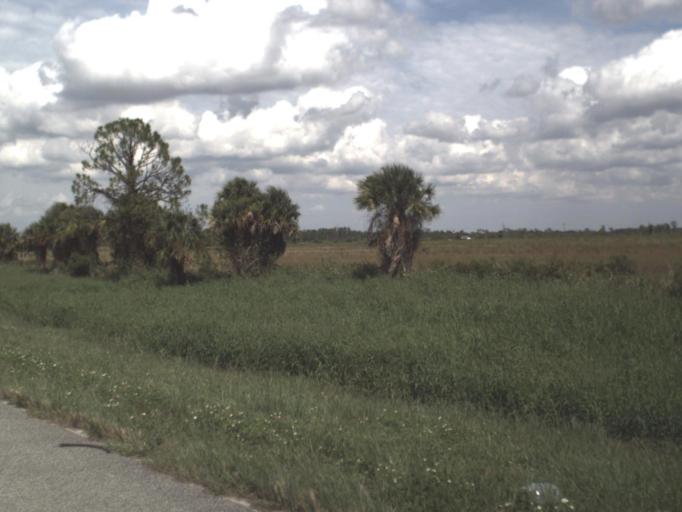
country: US
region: Florida
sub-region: Hendry County
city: Port LaBelle
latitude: 26.5924
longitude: -81.4367
